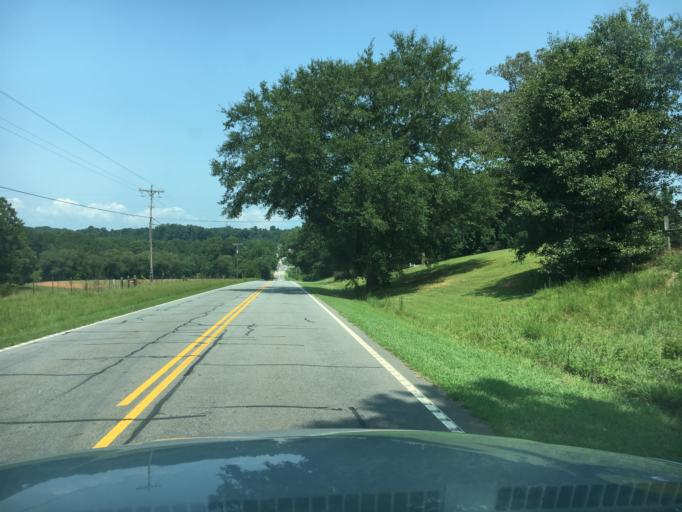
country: US
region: South Carolina
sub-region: Pickens County
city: Central
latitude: 34.7013
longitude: -82.7539
